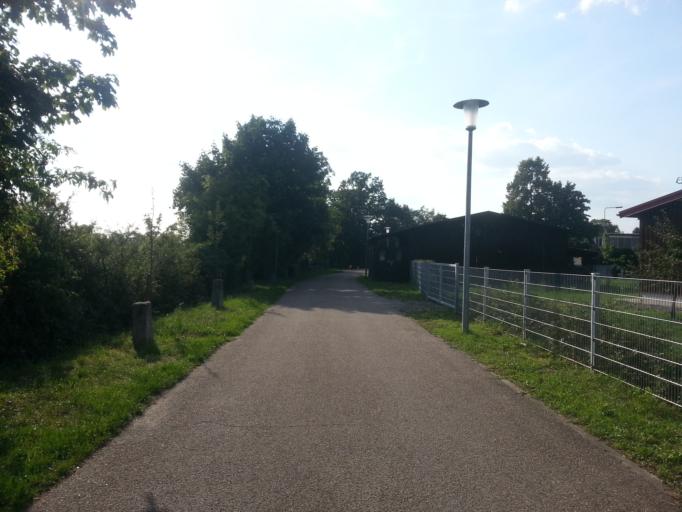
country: DE
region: Baden-Wuerttemberg
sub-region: Karlsruhe Region
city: Edingen-Neckarhausen
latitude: 49.4429
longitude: 8.6341
